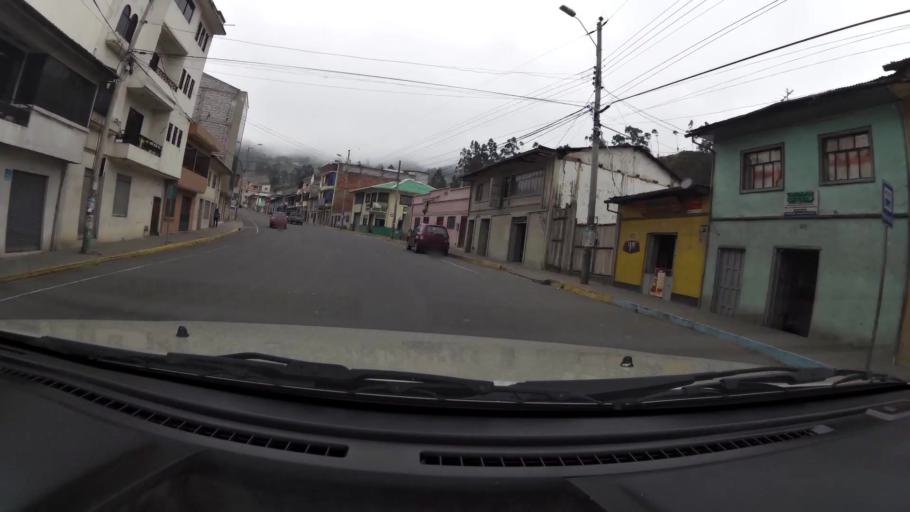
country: EC
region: Canar
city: Canar
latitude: -2.5082
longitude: -78.9255
